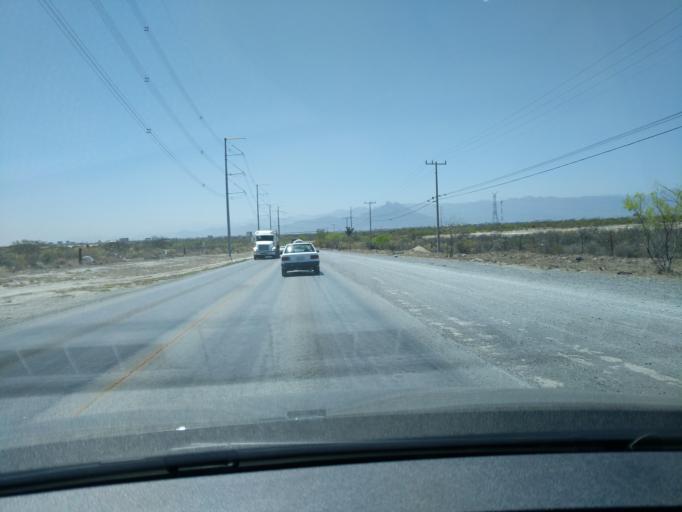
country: MX
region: Nuevo Leon
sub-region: Apodaca
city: Artemio Trevino
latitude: 25.8243
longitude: -100.1439
